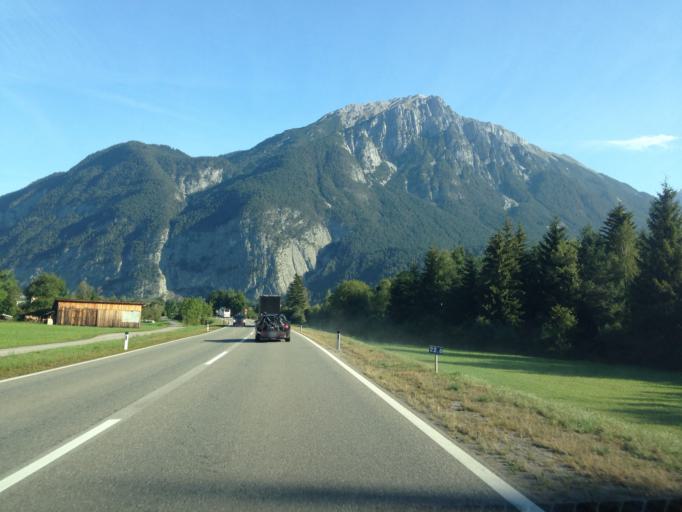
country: AT
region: Tyrol
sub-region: Politischer Bezirk Imst
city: Nassereith
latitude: 47.2983
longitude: 10.8438
